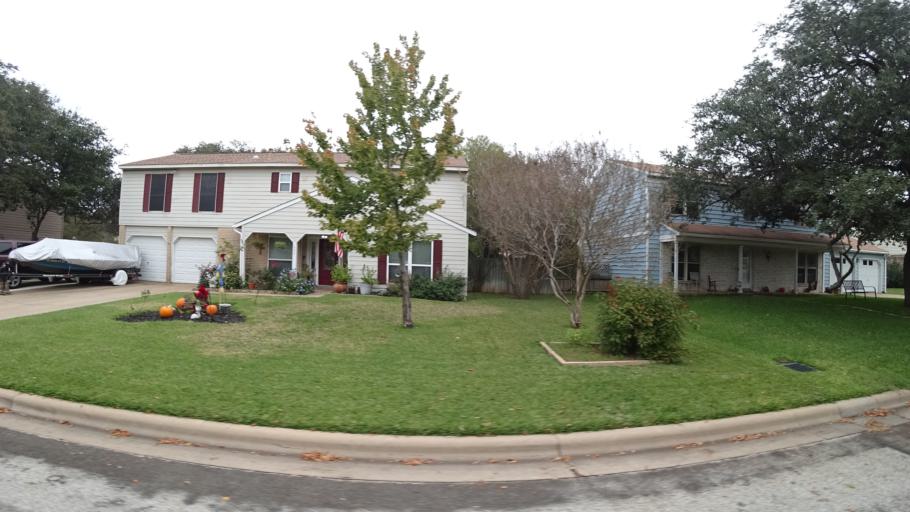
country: US
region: Texas
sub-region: Williamson County
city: Round Rock
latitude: 30.4907
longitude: -97.7002
